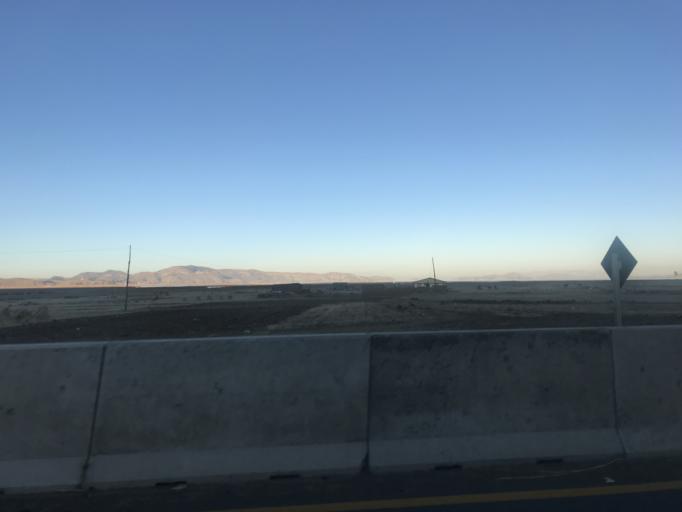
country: BO
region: La Paz
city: Batallas
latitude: -16.2465
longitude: -68.5701
